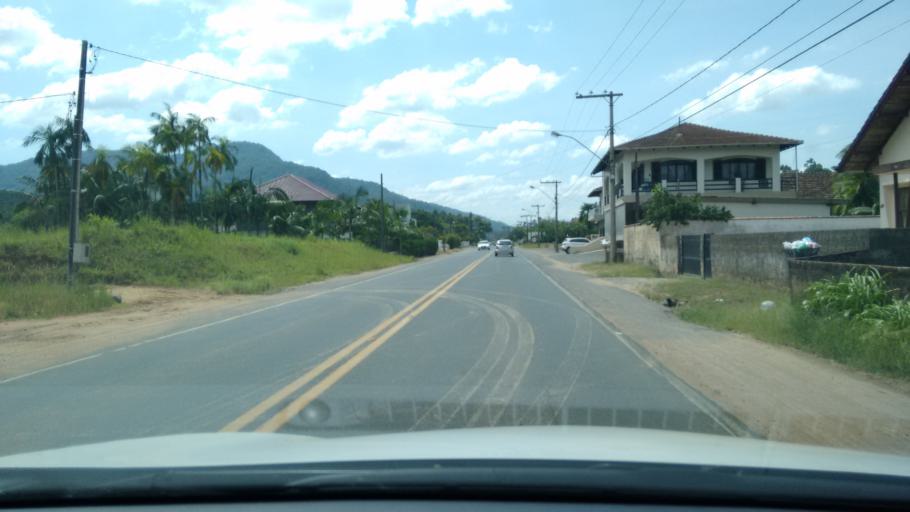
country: BR
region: Santa Catarina
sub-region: Timbo
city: Timbo
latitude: -26.8446
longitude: -49.3265
